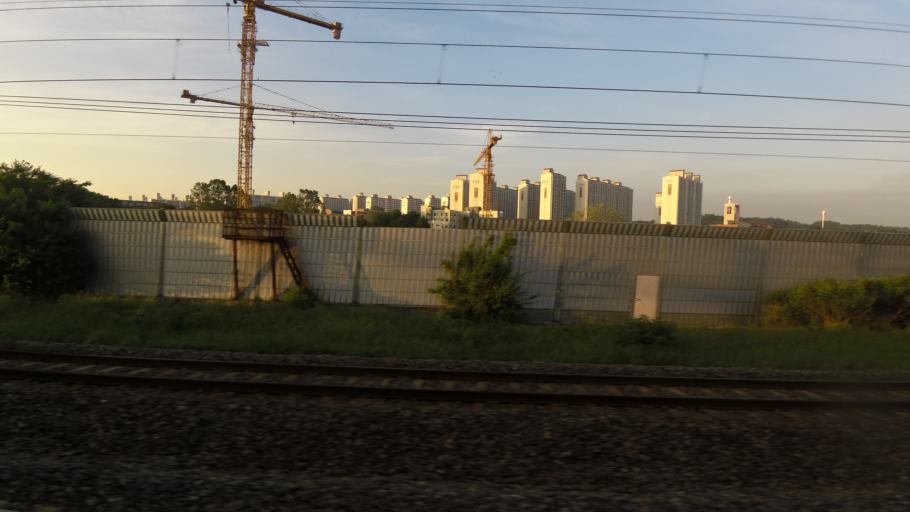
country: KR
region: Gyeonggi-do
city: Osan
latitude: 37.0461
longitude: 127.0548
